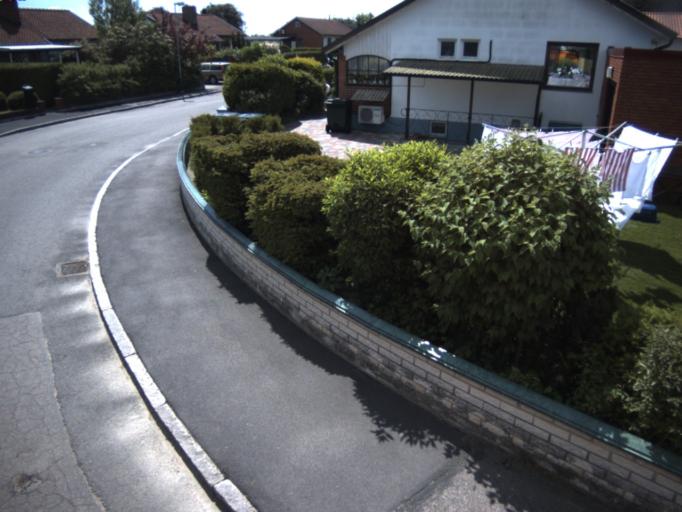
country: SE
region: Skane
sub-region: Helsingborg
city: Barslov
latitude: 56.0313
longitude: 12.8152
